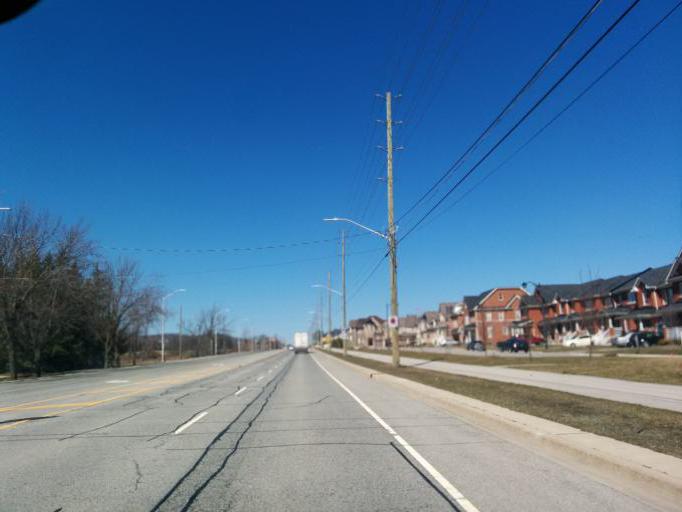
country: CA
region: Ontario
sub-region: Halton
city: Milton
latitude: 43.4892
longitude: -79.8883
